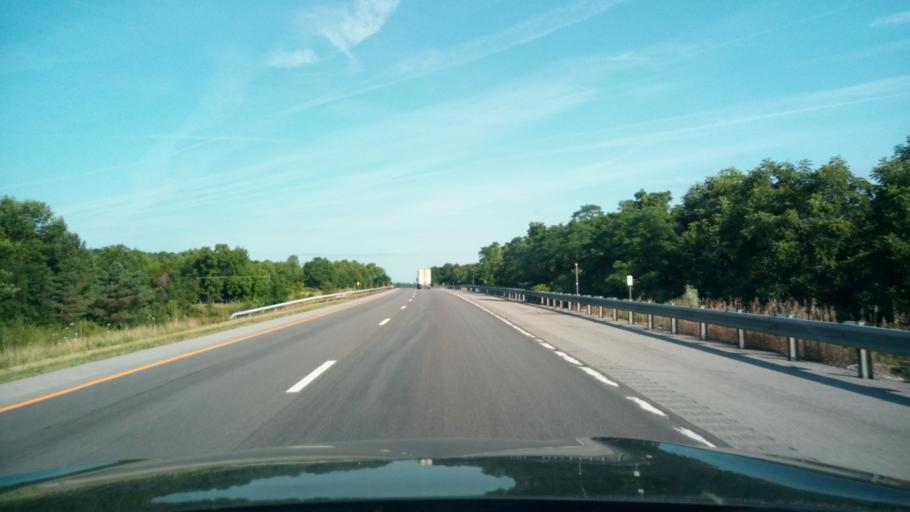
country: US
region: New York
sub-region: Livingston County
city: Mount Morris
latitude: 42.6427
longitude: -77.7899
